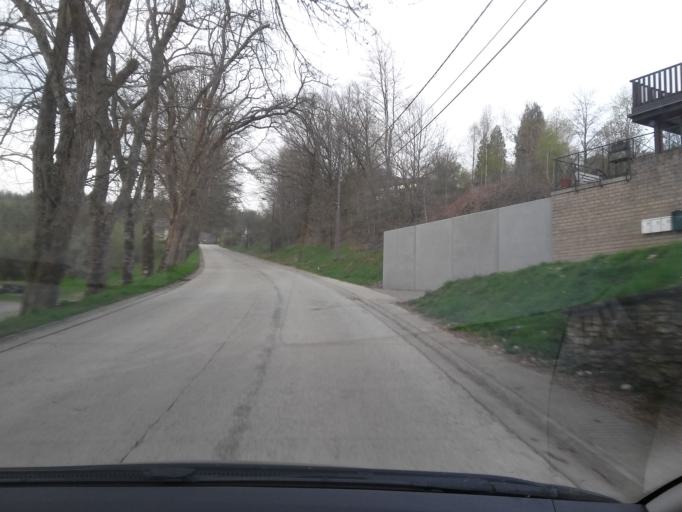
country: BE
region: Wallonia
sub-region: Province du Luxembourg
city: Herbeumont
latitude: 49.7826
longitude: 5.2429
